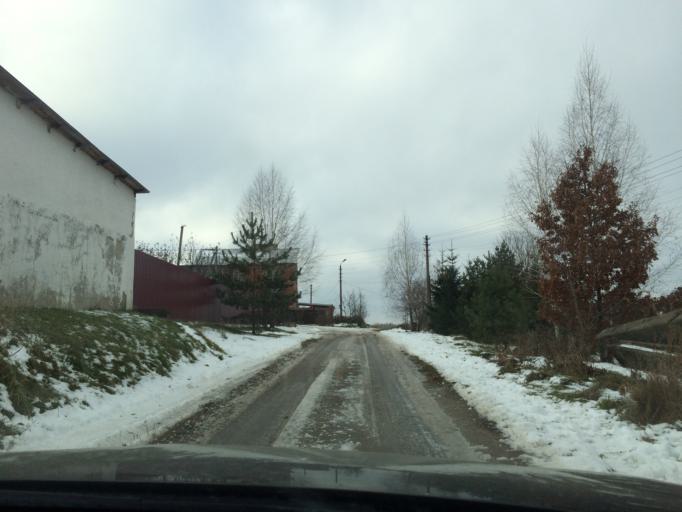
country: RU
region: Tula
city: Plavsk
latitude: 53.7068
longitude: 37.2719
